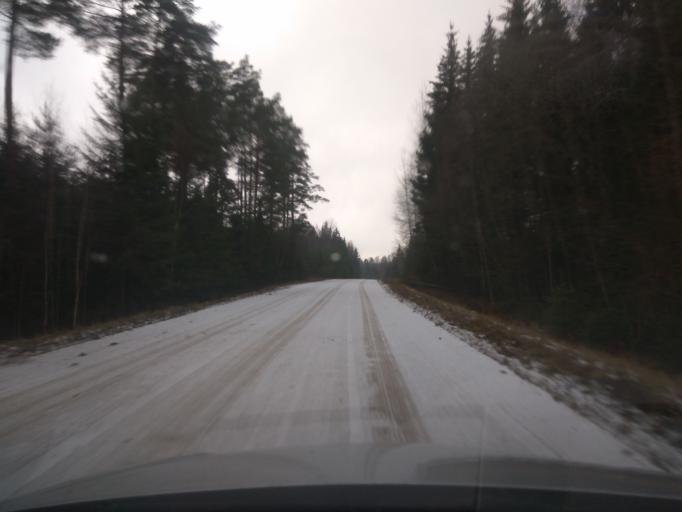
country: LV
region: Saldus Rajons
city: Saldus
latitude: 56.8176
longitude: 22.3441
